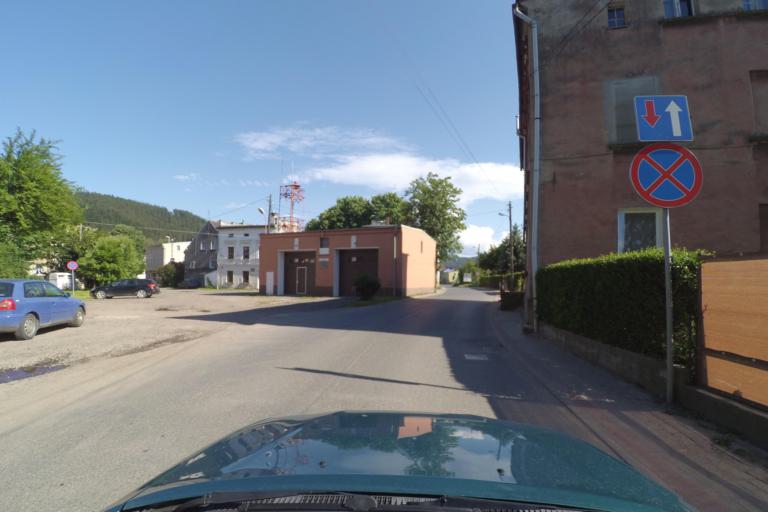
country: PL
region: Lower Silesian Voivodeship
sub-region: Powiat kamiennogorski
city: Lubawka
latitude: 50.7066
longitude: 15.9979
